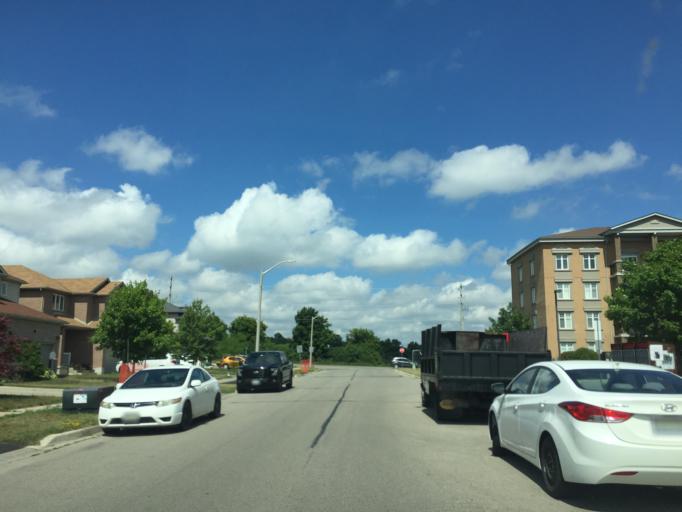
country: CA
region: Ontario
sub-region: Wellington County
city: Guelph
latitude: 43.5213
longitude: -80.1876
